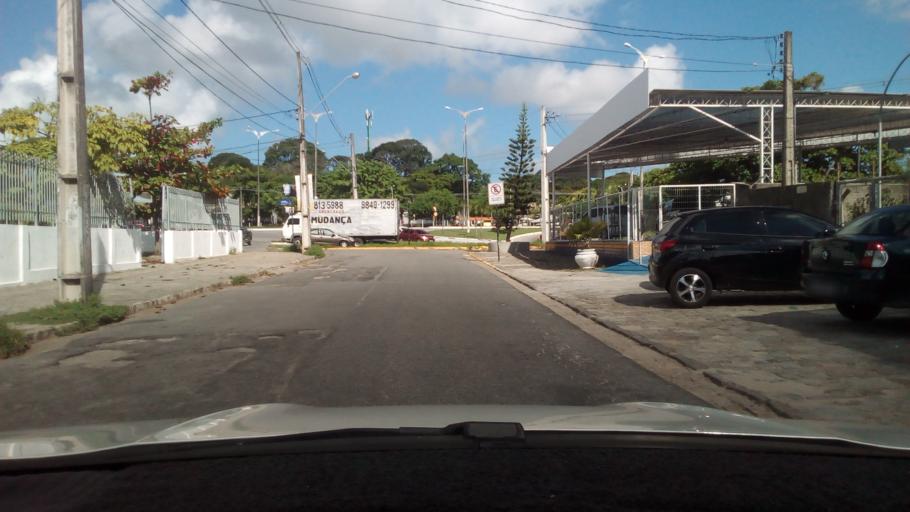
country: BR
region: Paraiba
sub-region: Joao Pessoa
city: Joao Pessoa
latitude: -7.1367
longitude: -34.8516
